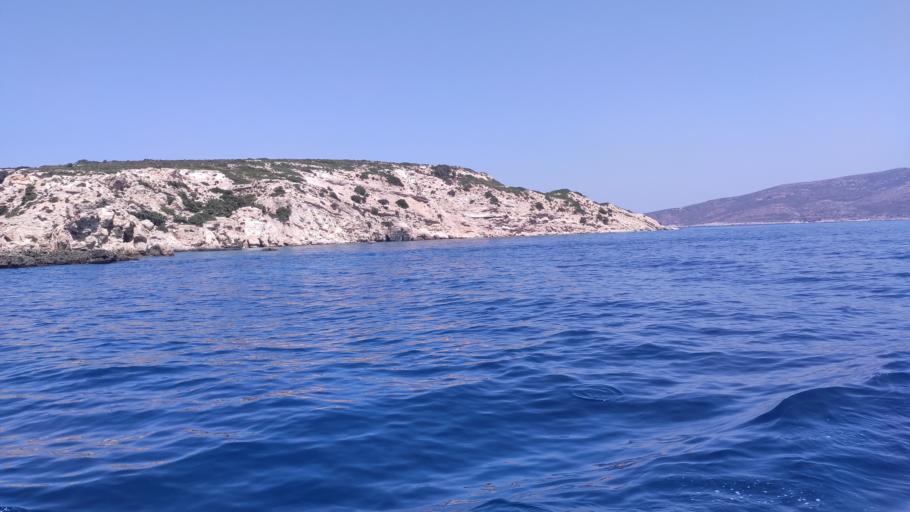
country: GR
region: South Aegean
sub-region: Nomos Dodekanisou
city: Pylion
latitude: 36.9322
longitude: 27.0954
